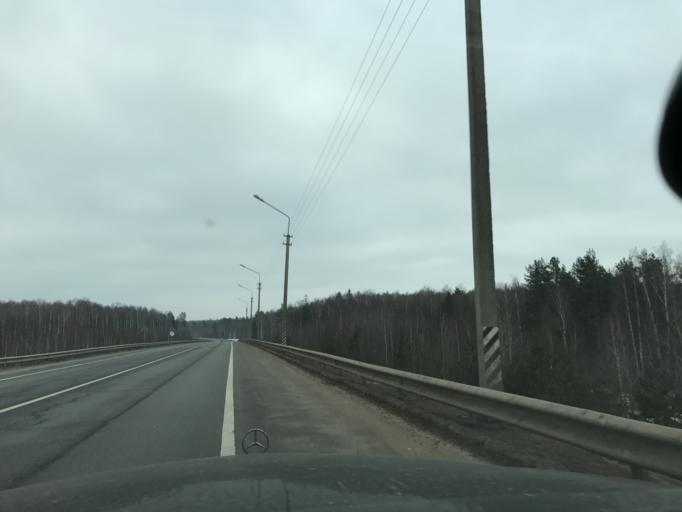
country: RU
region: Vladimir
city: Vorsha
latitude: 56.0750
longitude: 40.2150
